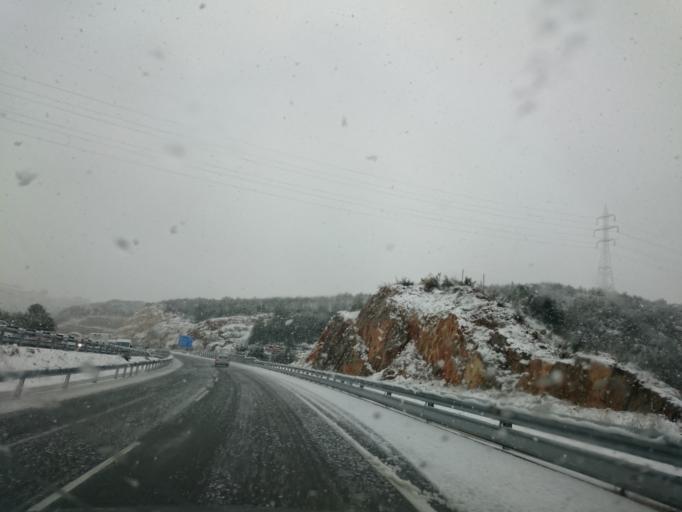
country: ES
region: Catalonia
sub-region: Provincia de Barcelona
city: Vilafranca del Penedes
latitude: 41.3046
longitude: 1.7219
